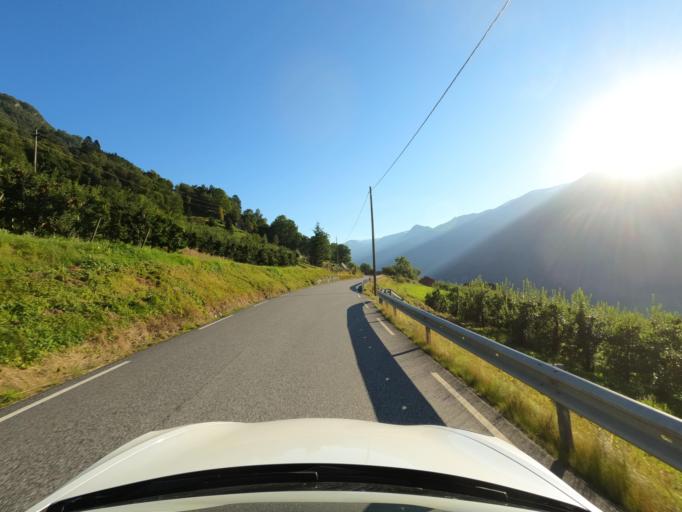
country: NO
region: Hordaland
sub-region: Ullensvang
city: Kinsarvik
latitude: 60.2326
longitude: 6.6149
